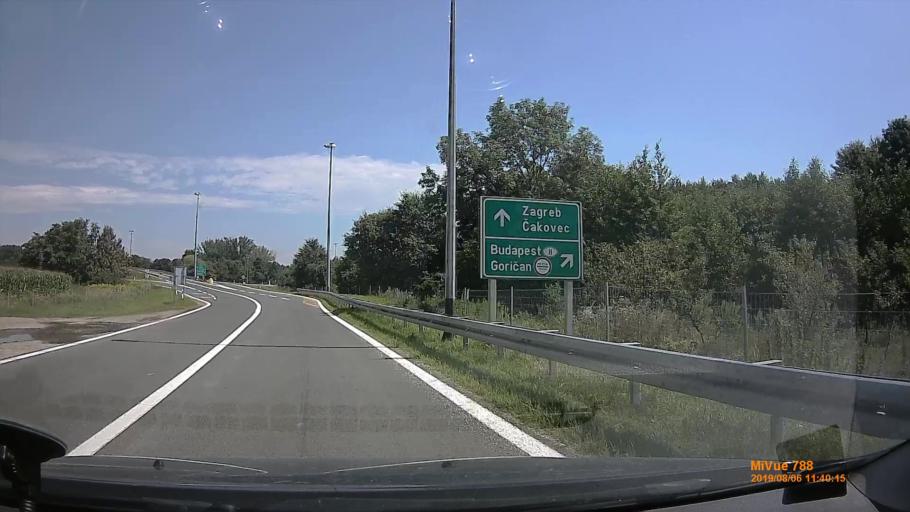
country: HR
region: Medimurska
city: Hodosan
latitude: 46.4065
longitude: 16.6642
